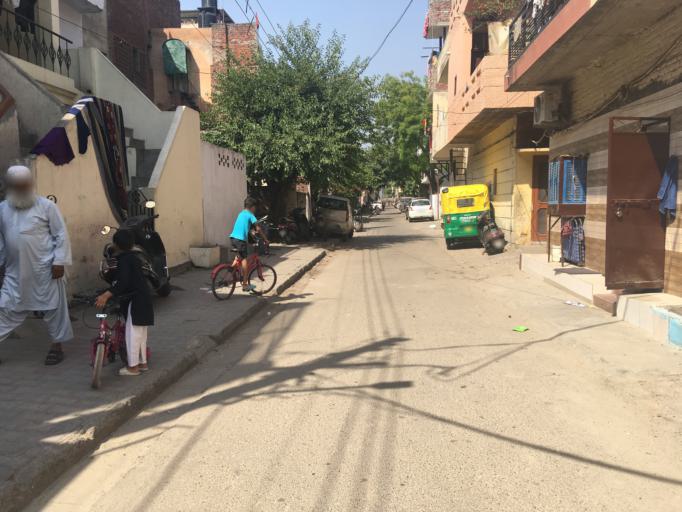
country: IN
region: Chandigarh
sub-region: Chandigarh
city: Chandigarh
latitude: 30.7089
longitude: 76.7939
